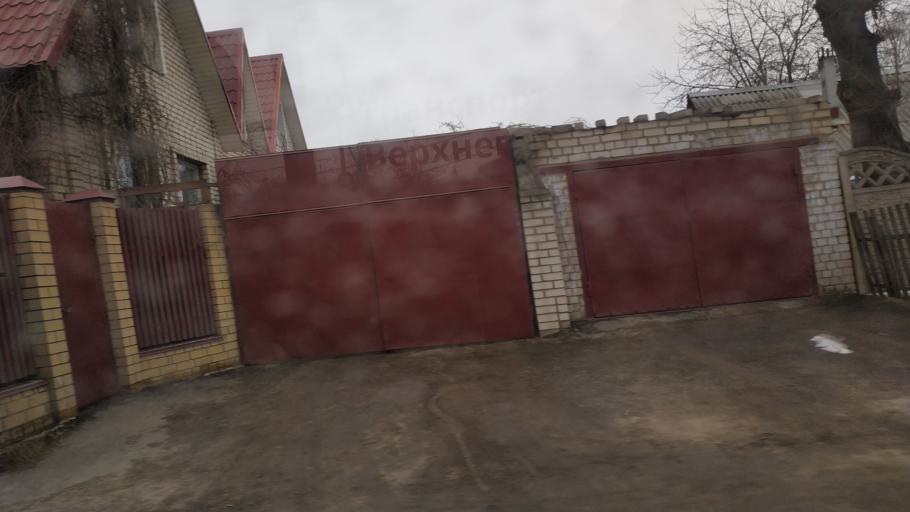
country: RU
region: Tverskaya
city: Tver
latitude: 56.8807
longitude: 35.8997
